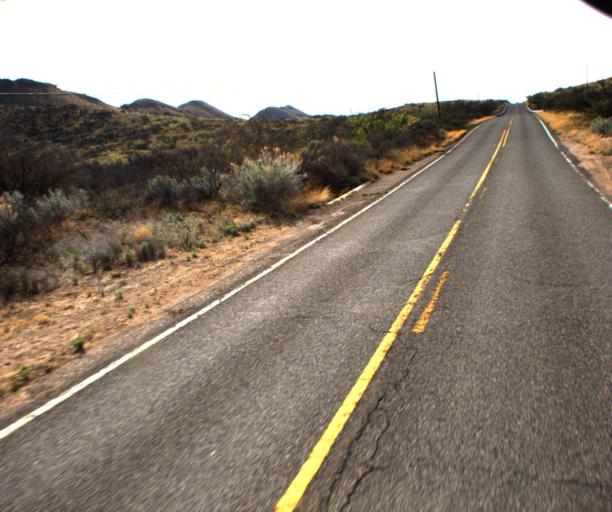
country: US
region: Arizona
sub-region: Cochise County
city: Willcox
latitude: 32.1709
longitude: -109.5972
